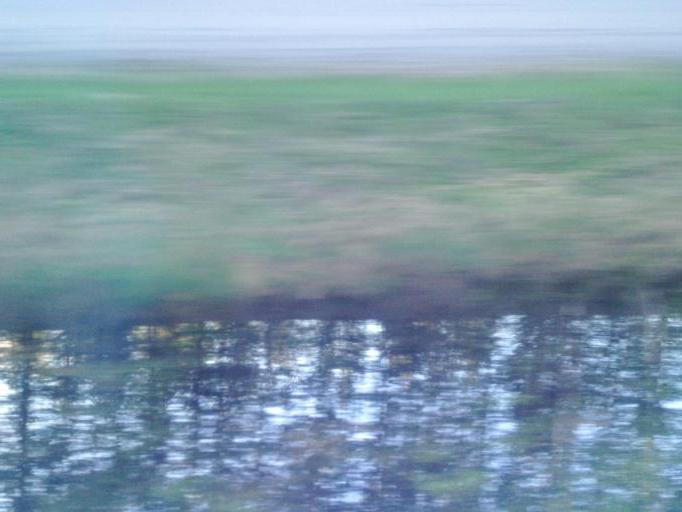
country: FI
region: Haeme
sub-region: Haemeenlinna
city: Parola
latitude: 61.0421
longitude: 24.3671
